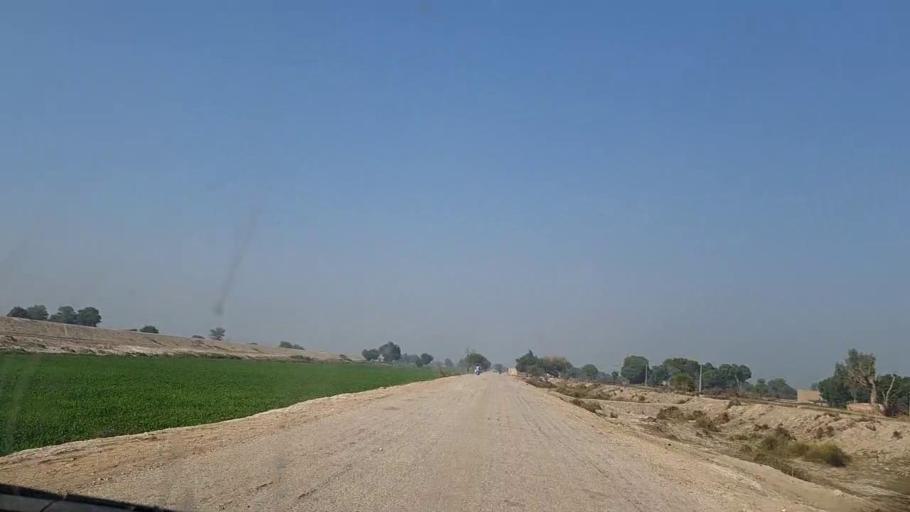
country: PK
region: Sindh
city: Moro
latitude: 26.7287
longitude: 67.9211
